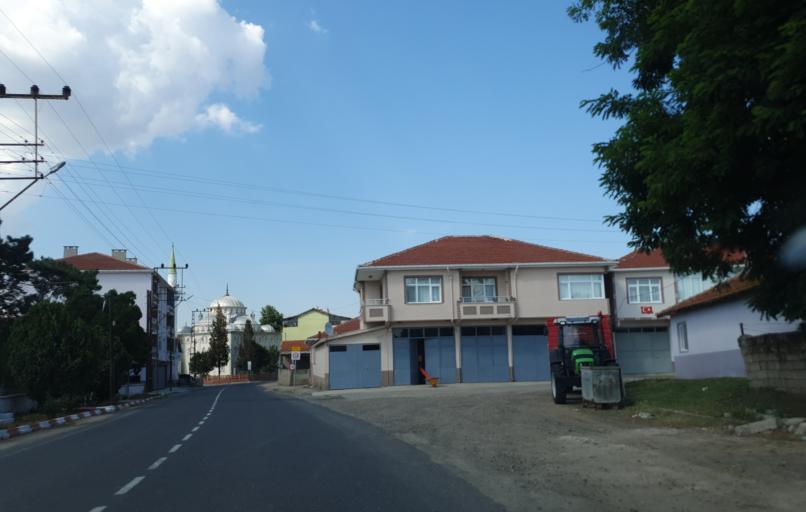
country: TR
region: Tekirdag
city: Muratli
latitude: 41.2192
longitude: 27.5443
